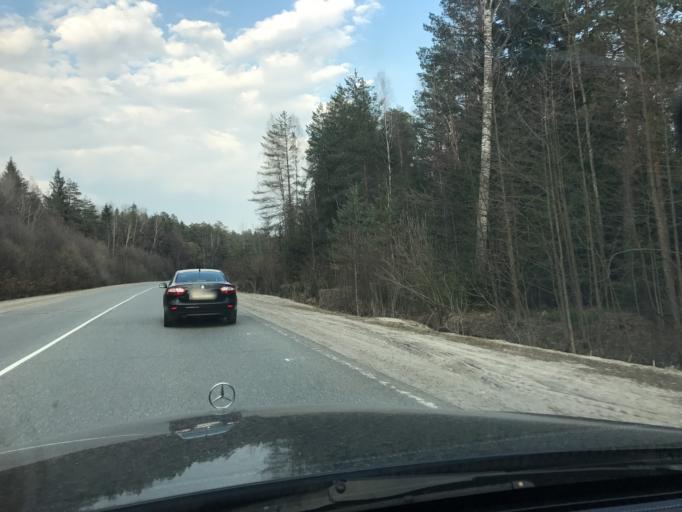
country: RU
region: Vladimir
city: Muromtsevo
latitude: 55.9580
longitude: 40.9725
